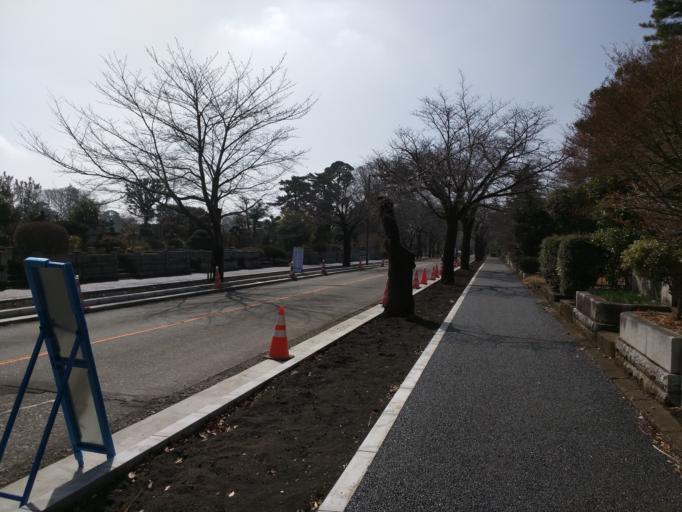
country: JP
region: Tokyo
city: Kokubunji
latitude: 35.6872
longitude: 139.5124
